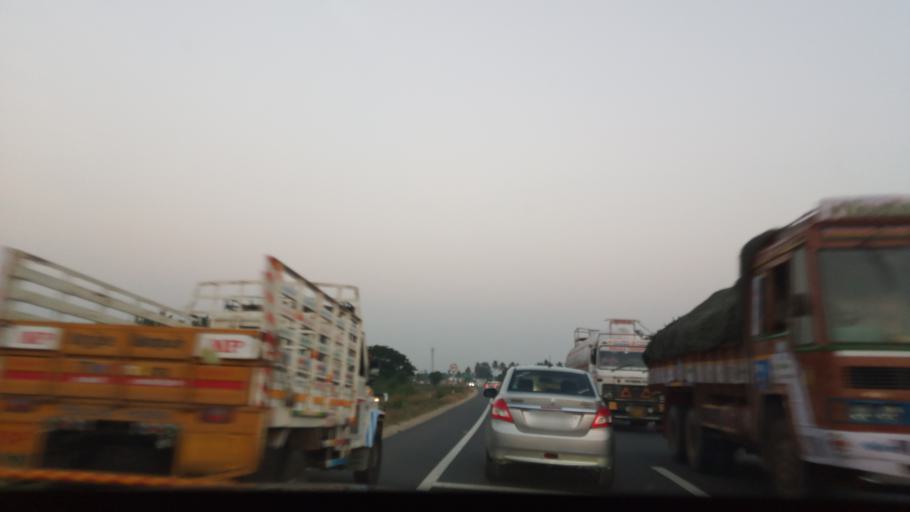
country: IN
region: Tamil Nadu
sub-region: Salem
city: Belur
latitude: 11.6499
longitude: 78.3947
